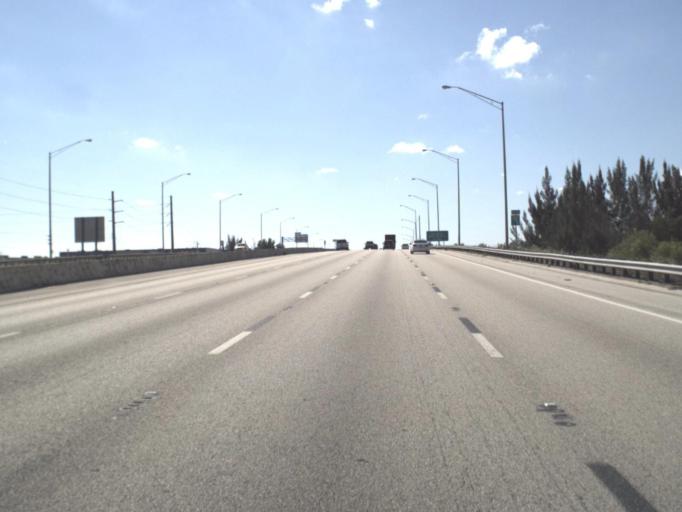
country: US
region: Florida
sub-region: Miami-Dade County
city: Doral
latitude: 25.7998
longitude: -80.3862
